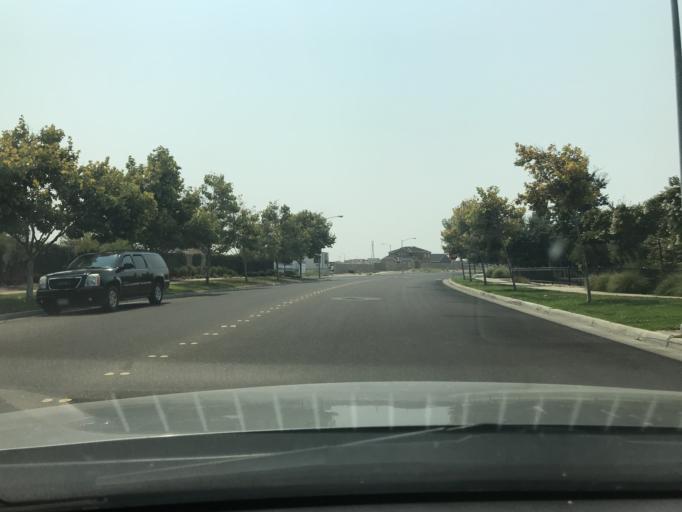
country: US
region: California
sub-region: Merced County
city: Merced
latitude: 37.3536
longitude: -120.4720
